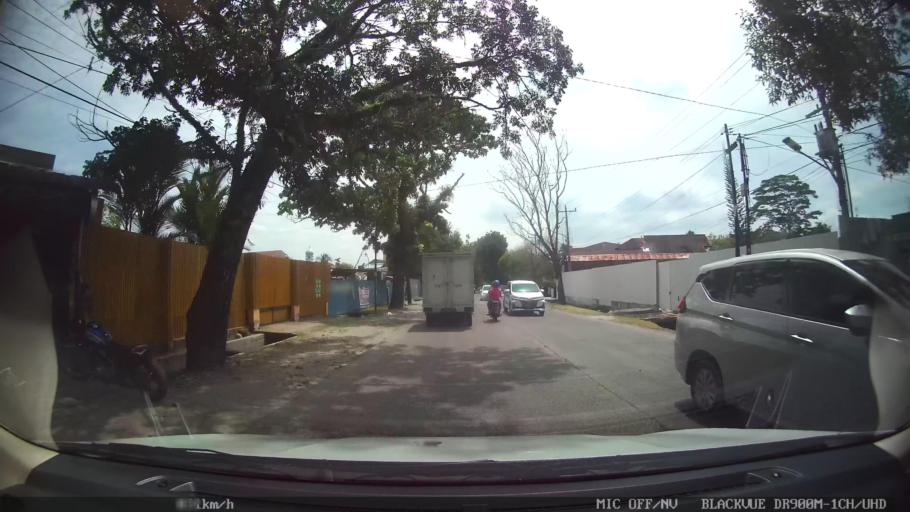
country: ID
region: North Sumatra
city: Sunggal
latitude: 3.5809
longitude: 98.6379
